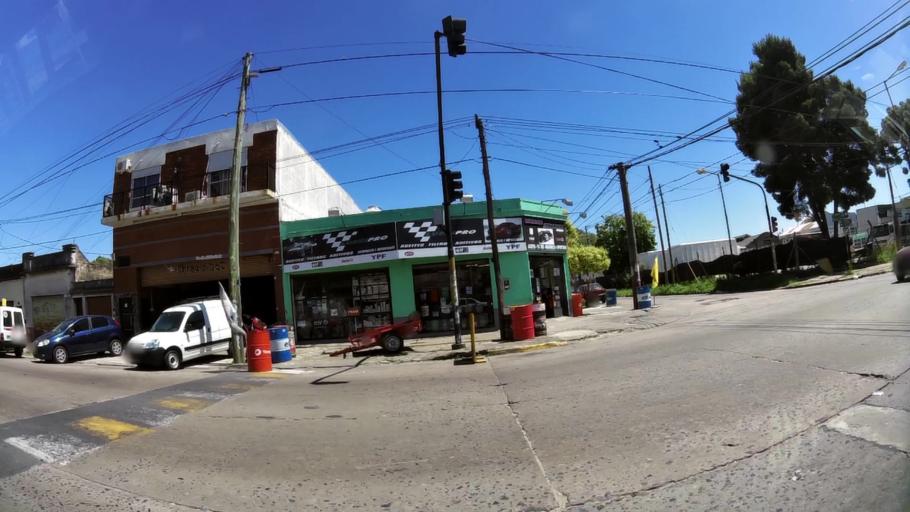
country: AR
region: Buenos Aires
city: Caseros
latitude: -34.5795
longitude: -58.5520
